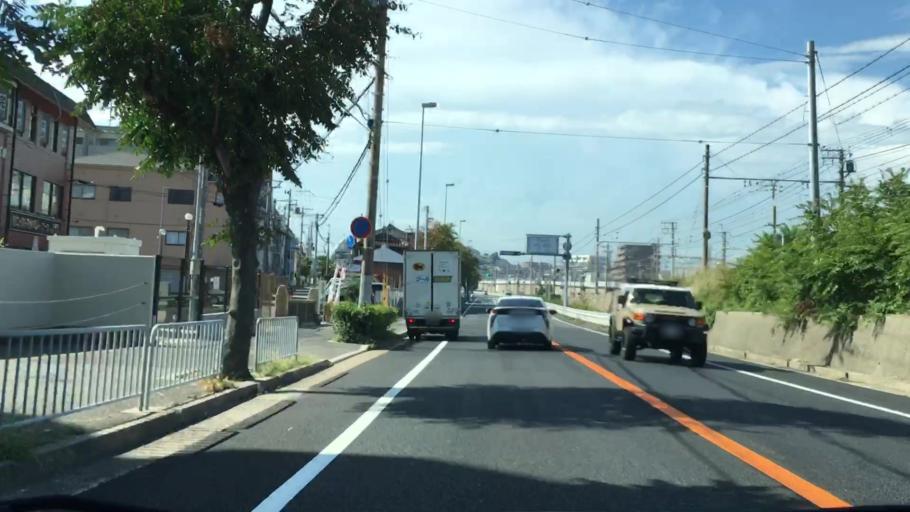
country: JP
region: Hyogo
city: Akashi
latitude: 34.6352
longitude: 135.0311
